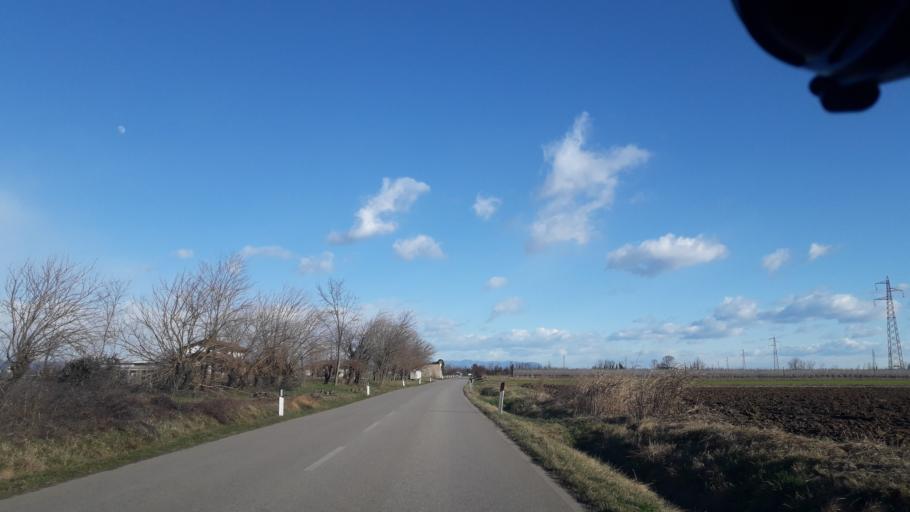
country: IT
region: Friuli Venezia Giulia
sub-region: Provincia di Udine
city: Martignacco
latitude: 46.0759
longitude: 13.1540
